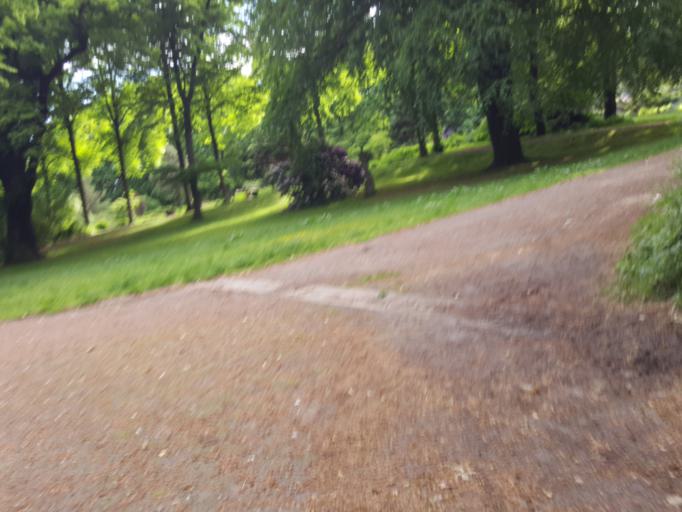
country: DE
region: Hamburg
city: Borgfelde
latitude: 53.5582
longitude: 10.0580
